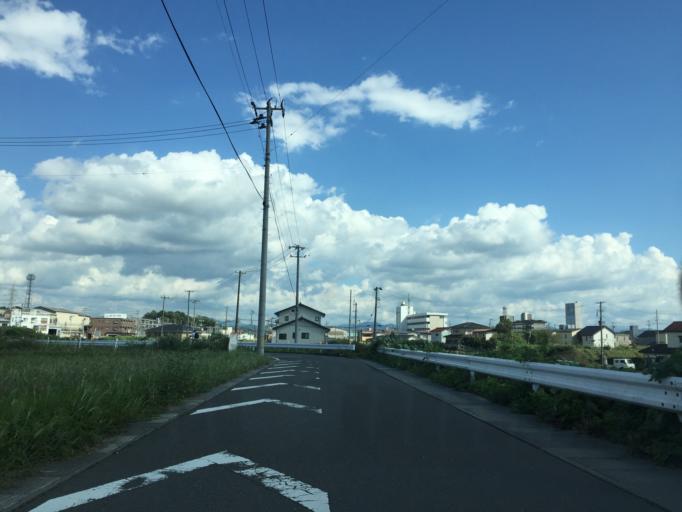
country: JP
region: Fukushima
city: Koriyama
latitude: 37.4128
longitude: 140.3749
